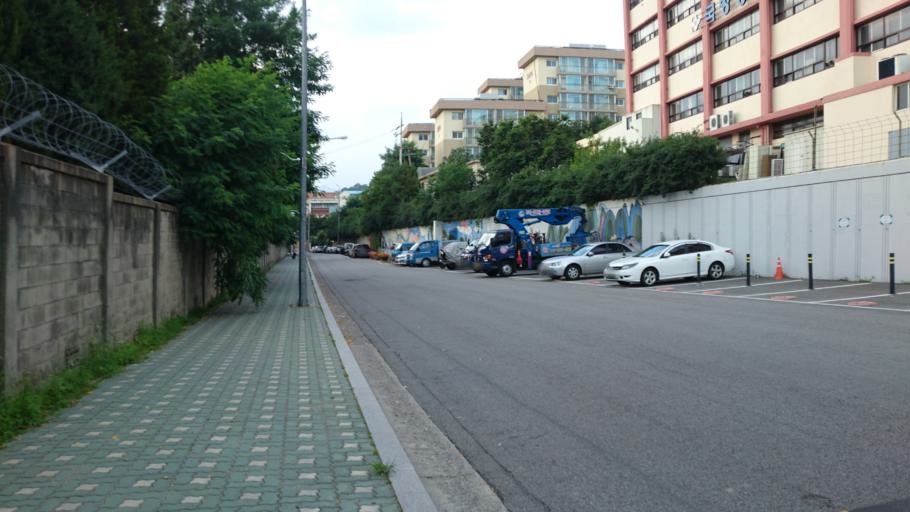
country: KR
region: Seoul
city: Seoul
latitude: 37.5429
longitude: 126.9792
